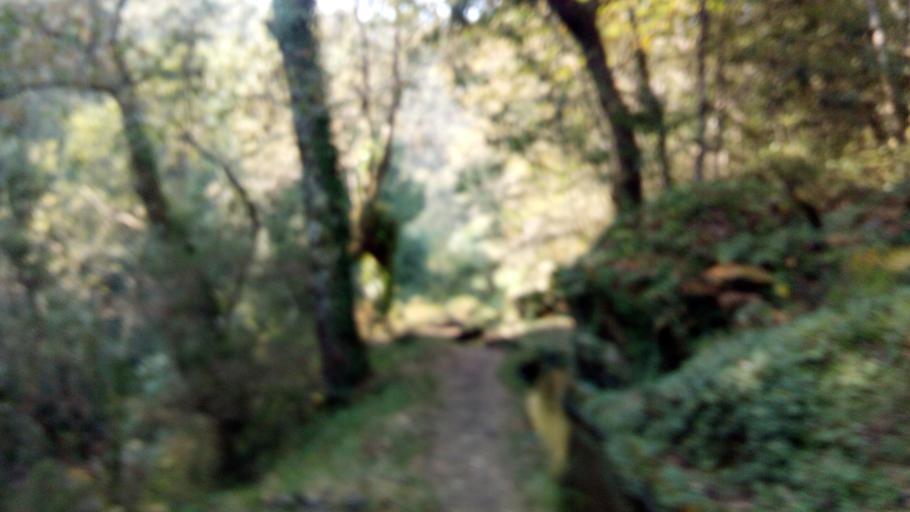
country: ES
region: Galicia
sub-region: Provincia de Pontevedra
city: Oia
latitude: 41.9969
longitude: -8.8136
